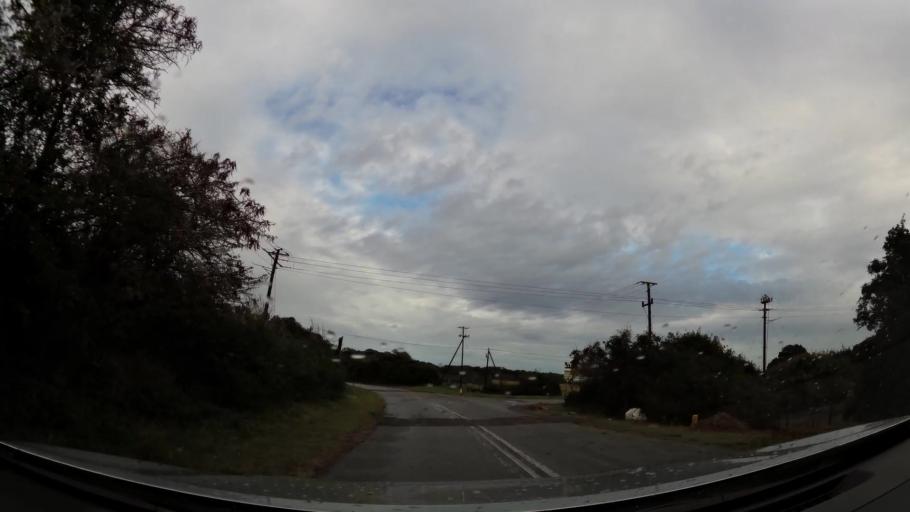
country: ZA
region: Eastern Cape
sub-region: Nelson Mandela Bay Metropolitan Municipality
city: Port Elizabeth
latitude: -34.0175
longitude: 25.4986
